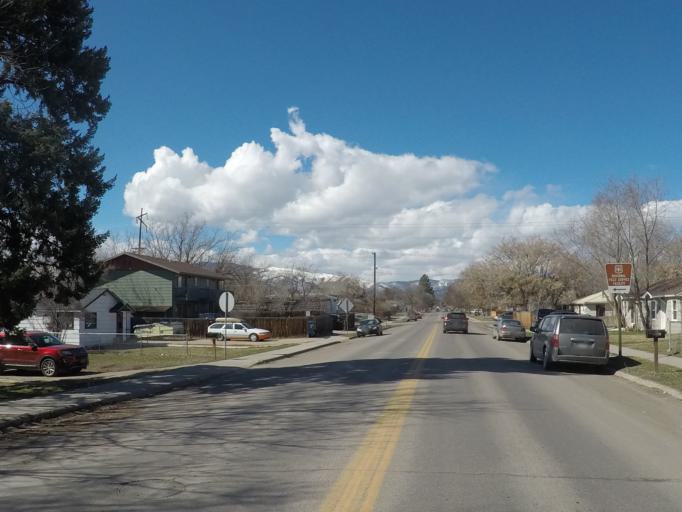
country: US
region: Montana
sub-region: Missoula County
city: Orchard Homes
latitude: 46.8566
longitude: -114.0212
